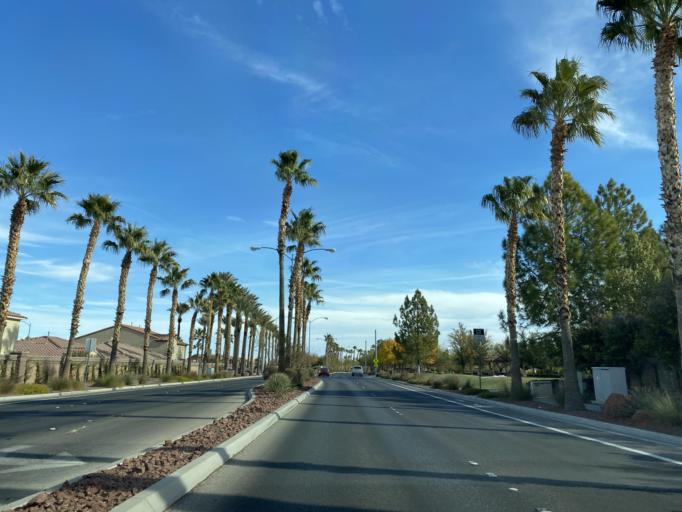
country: US
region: Nevada
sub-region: Clark County
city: Enterprise
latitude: 36.0484
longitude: -115.2574
